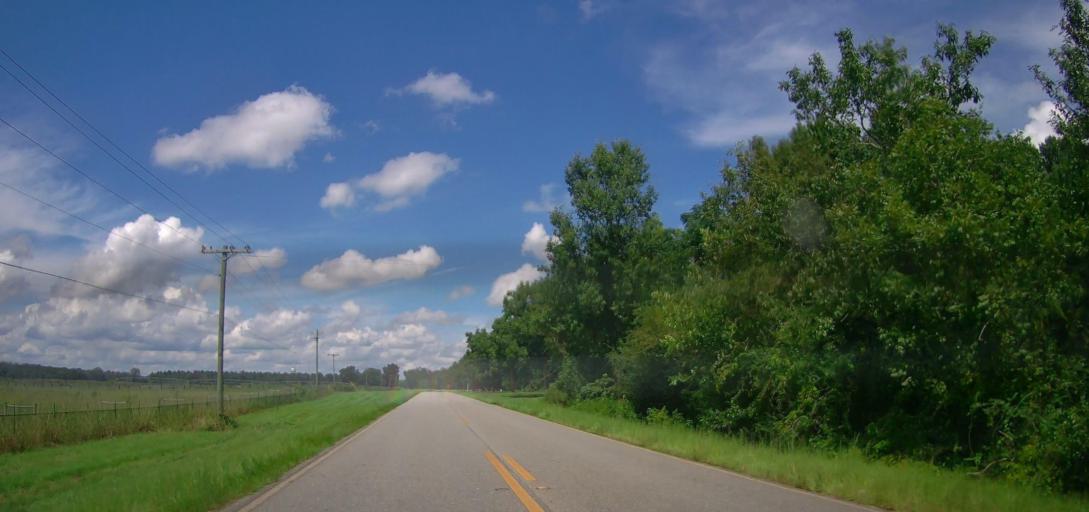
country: US
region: Georgia
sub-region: Peach County
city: Fort Valley
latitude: 32.5131
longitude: -83.8647
